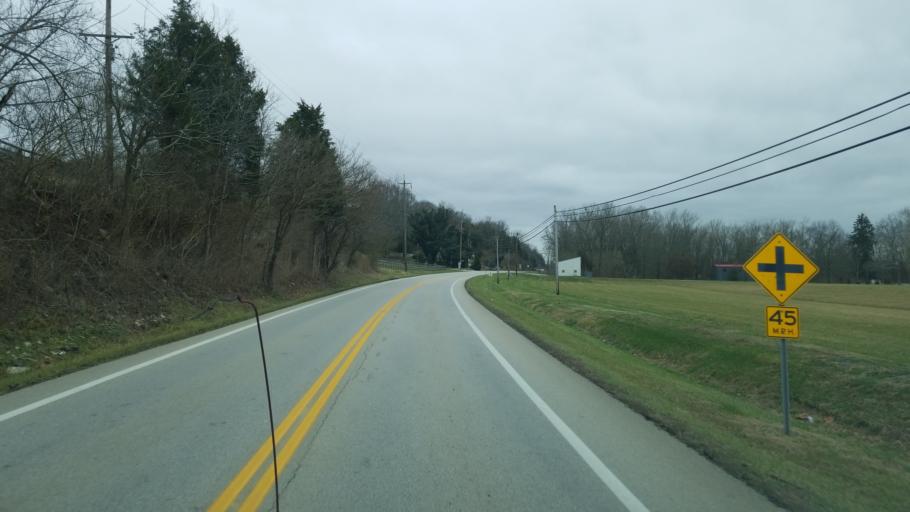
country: US
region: Ohio
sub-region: Clermont County
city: New Richmond
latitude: 38.9242
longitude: -84.2548
